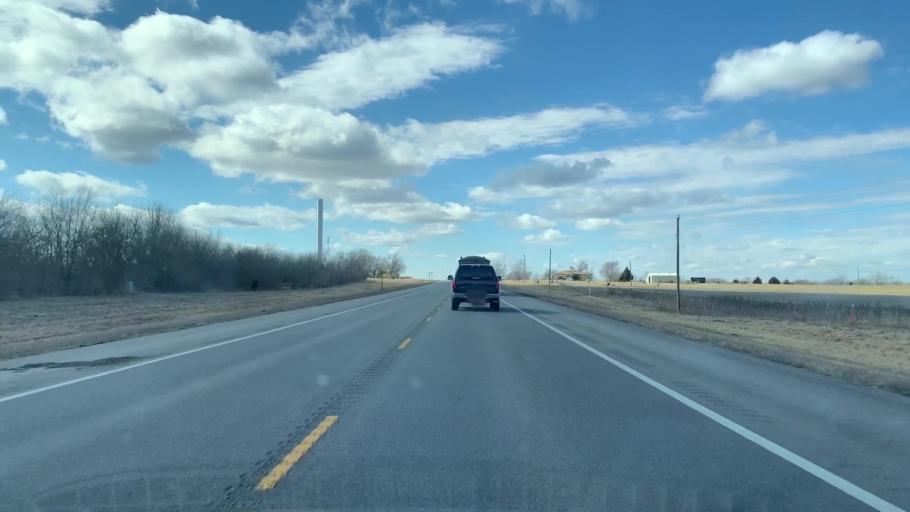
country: US
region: Kansas
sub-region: Cherokee County
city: Columbus
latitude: 37.3400
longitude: -94.9020
